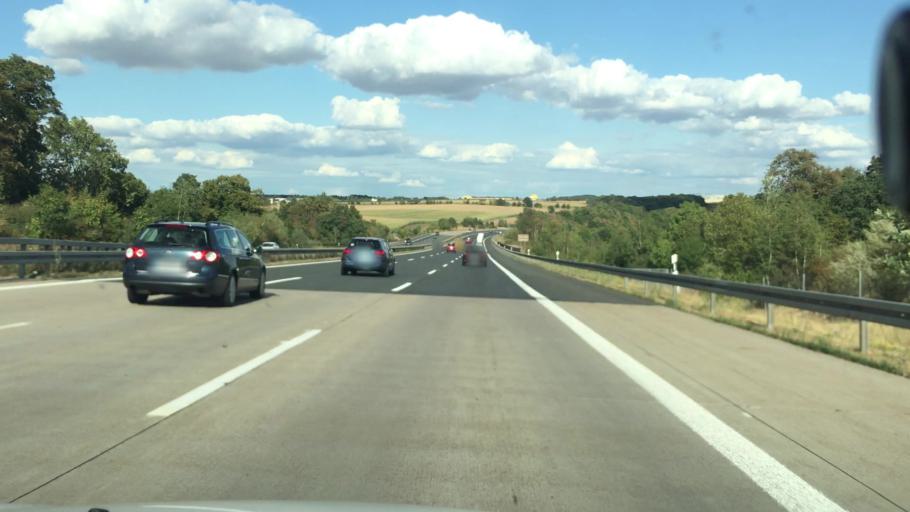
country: DE
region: Saxony
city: Hainichen
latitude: 50.9994
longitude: 13.1590
